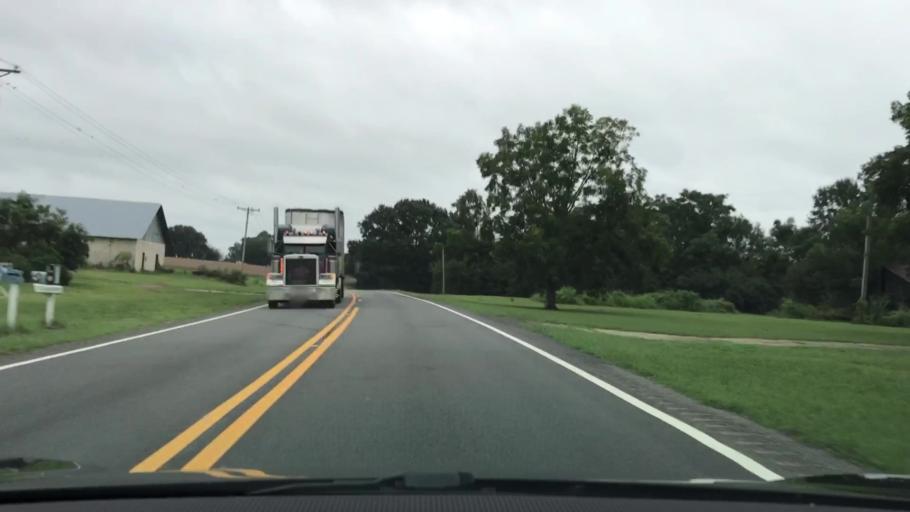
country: US
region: Alabama
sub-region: Covington County
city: Opp
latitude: 31.2736
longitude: -86.1585
